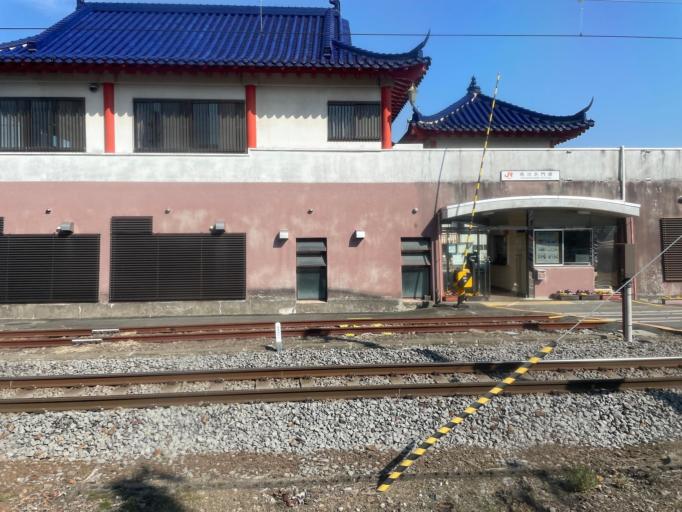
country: JP
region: Yamanashi
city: Ryuo
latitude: 35.5604
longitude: 138.4927
